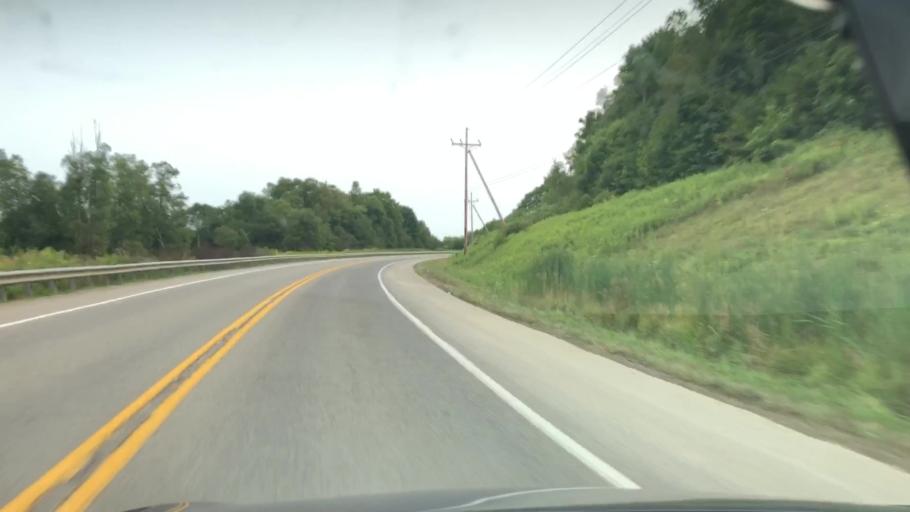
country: US
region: Pennsylvania
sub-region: Venango County
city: Hasson Heights
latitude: 41.5257
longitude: -79.7113
